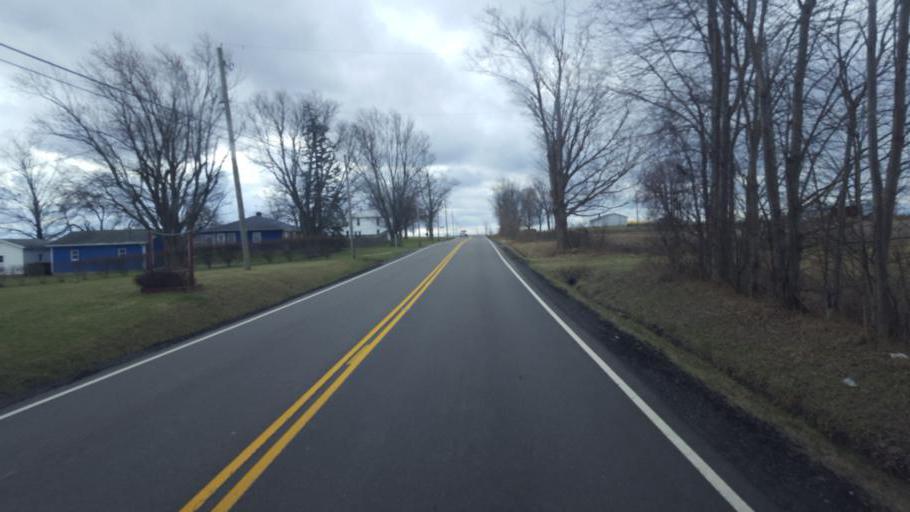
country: US
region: Ohio
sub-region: Licking County
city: Utica
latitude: 40.3042
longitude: -82.5113
